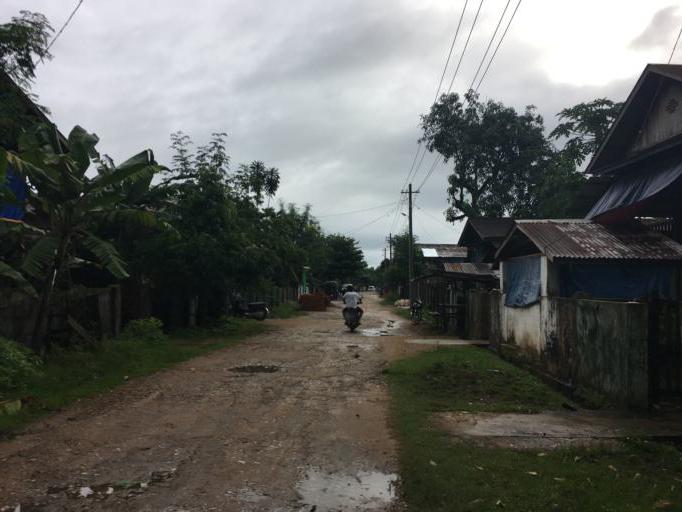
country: MM
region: Mon
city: Mudon
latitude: 16.0392
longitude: 98.1182
